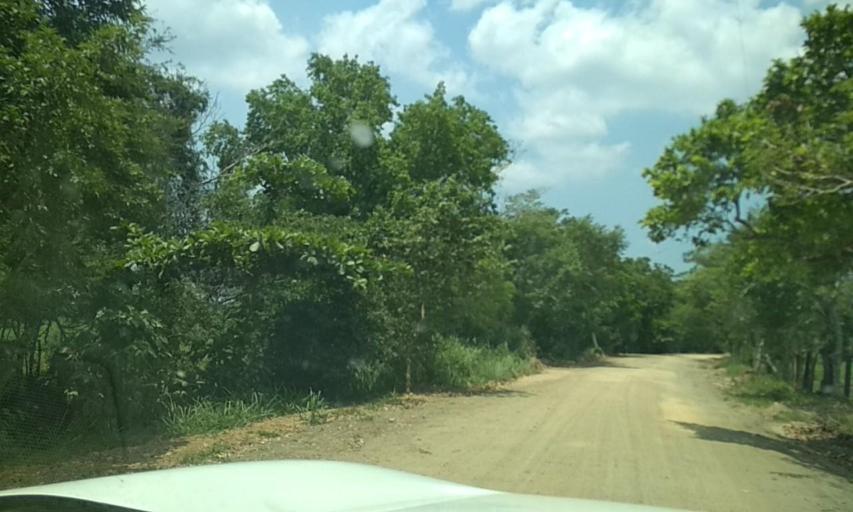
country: MX
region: Veracruz
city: Las Choapas
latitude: 17.9162
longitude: -94.0865
